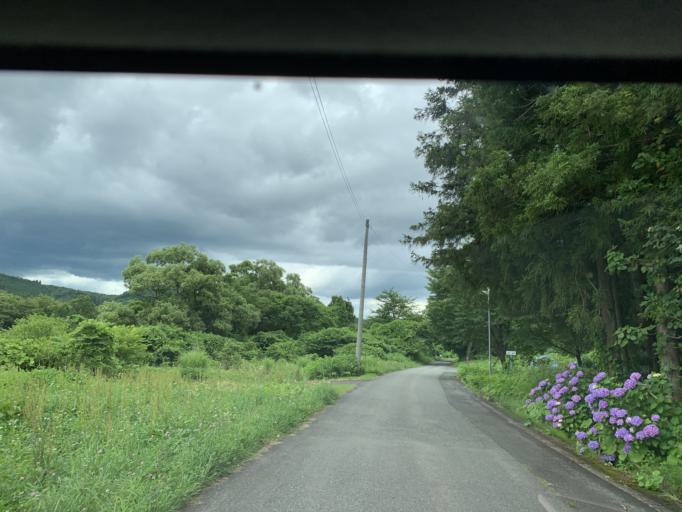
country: JP
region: Iwate
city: Ichinoseki
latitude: 38.9683
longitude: 140.9936
